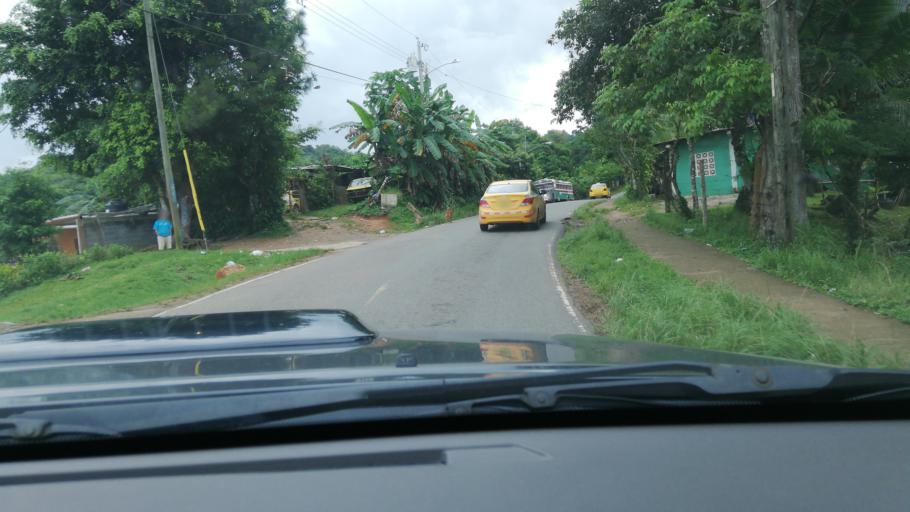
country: PA
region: Panama
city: Cerro Azul
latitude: 9.1100
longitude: -79.4448
